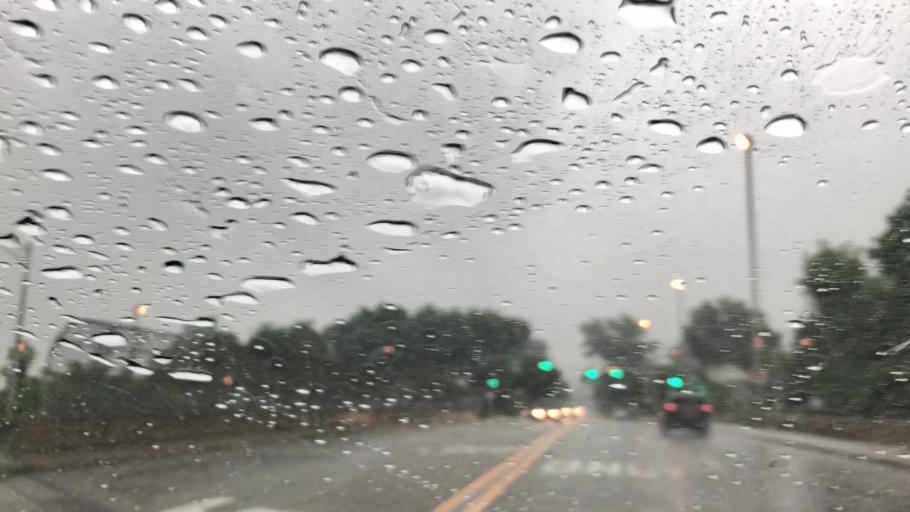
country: US
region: New Jersey
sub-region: Bergen County
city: Rochelle Park
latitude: 40.9131
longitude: -74.0716
